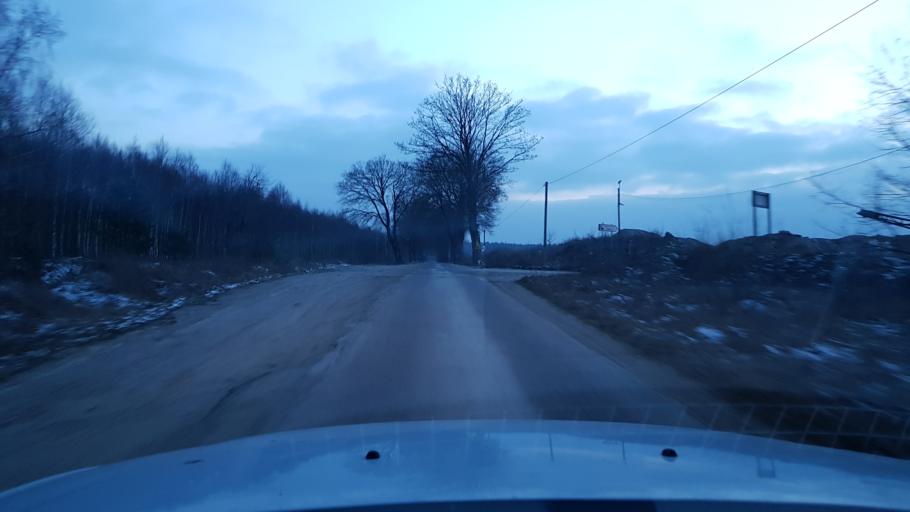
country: PL
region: West Pomeranian Voivodeship
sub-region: Powiat swidwinski
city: Slawoborze
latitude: 53.9262
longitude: 15.7243
